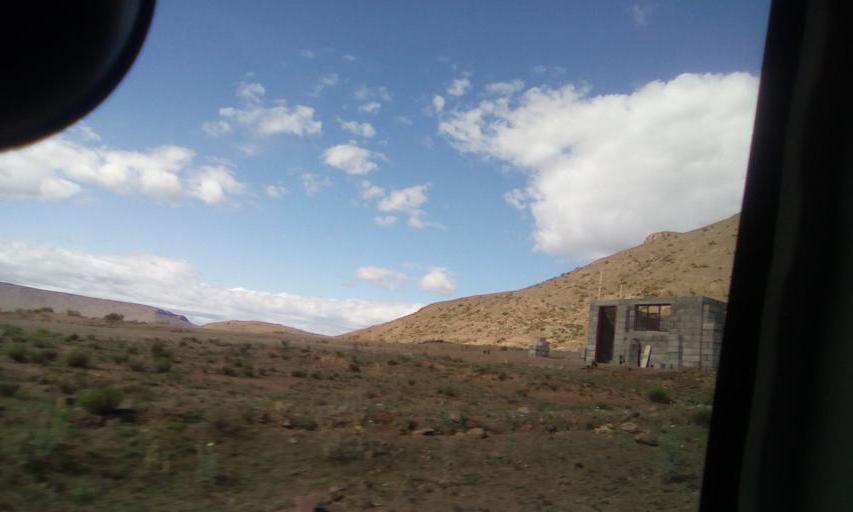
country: LS
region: Qacha's Nek
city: Qacha's Nek
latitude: -30.0098
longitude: 28.1767
